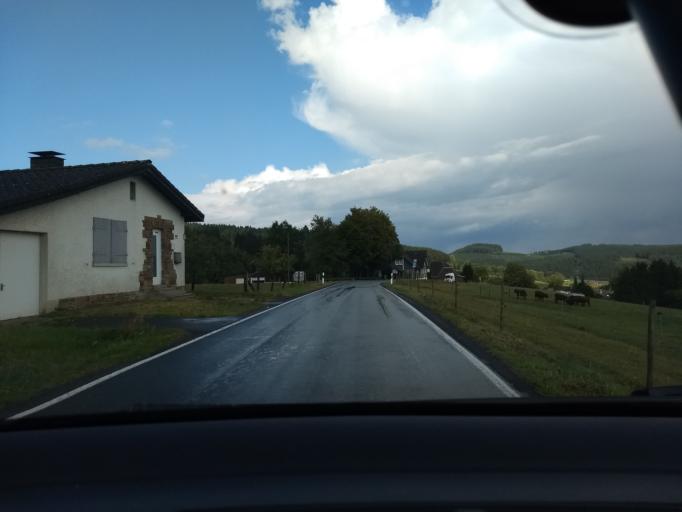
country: DE
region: North Rhine-Westphalia
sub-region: Regierungsbezirk Arnsberg
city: Finnentrop
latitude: 51.2217
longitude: 8.0279
